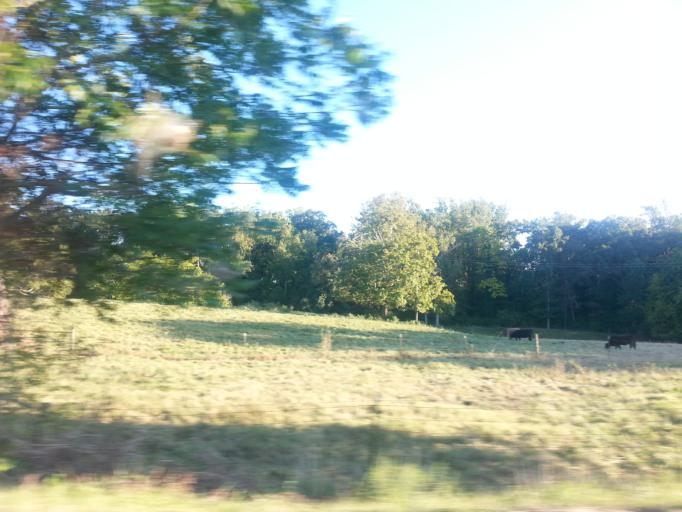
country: US
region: Tennessee
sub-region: Blount County
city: Alcoa
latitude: 35.8207
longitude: -84.0015
